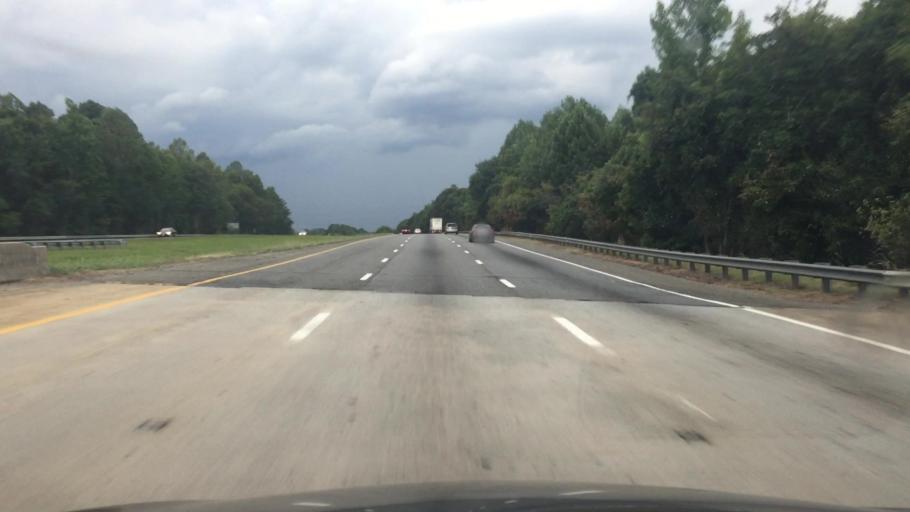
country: US
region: North Carolina
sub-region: Davidson County
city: Lexington
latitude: 35.7770
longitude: -80.2954
